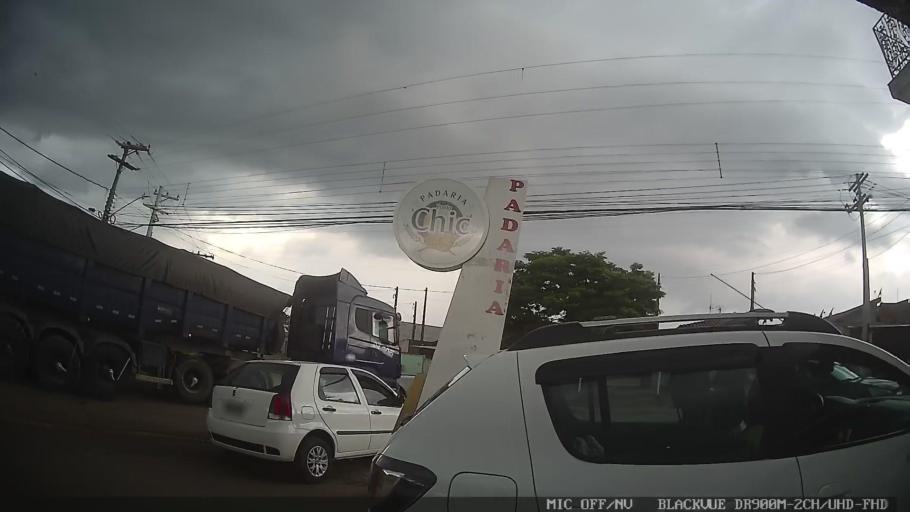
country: BR
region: Sao Paulo
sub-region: Atibaia
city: Atibaia
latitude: -23.1444
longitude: -46.5882
